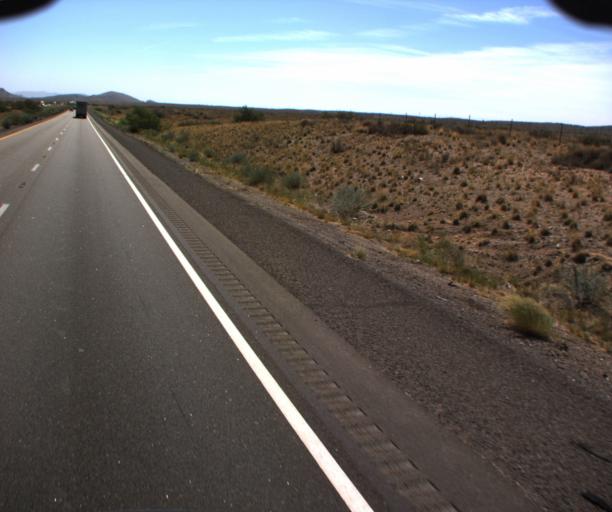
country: US
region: Arizona
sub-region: Mohave County
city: New Kingman-Butler
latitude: 35.1954
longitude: -113.8638
